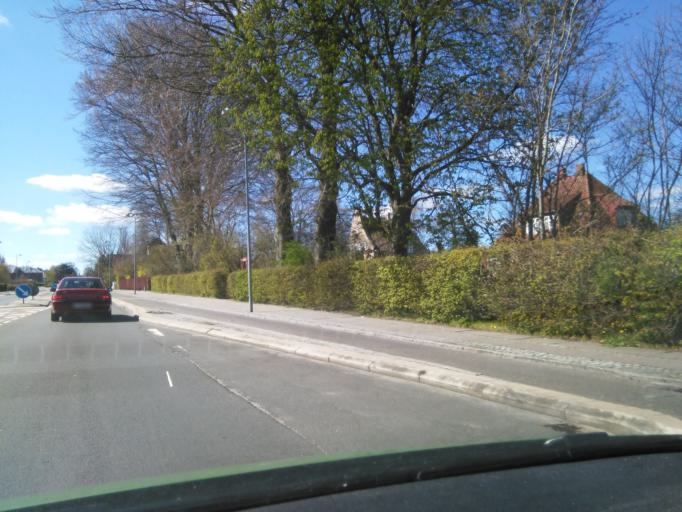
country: DK
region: Central Jutland
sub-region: Horsens Kommune
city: Horsens
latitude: 55.8497
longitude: 9.8282
